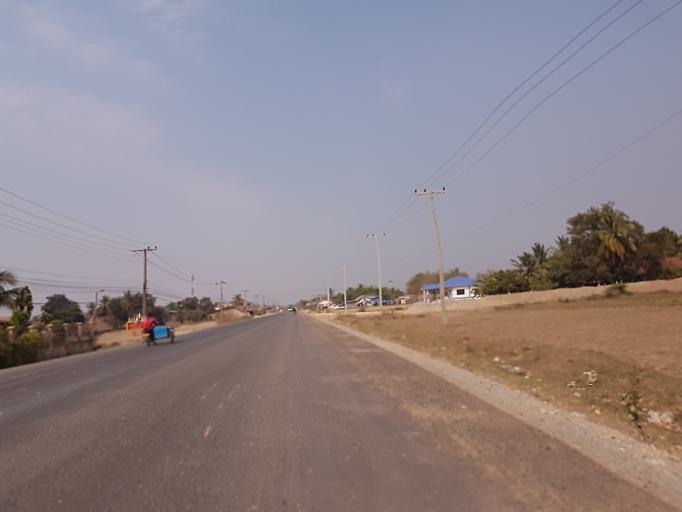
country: TH
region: Nong Khai
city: Nong Khai
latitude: 17.9190
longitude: 102.7671
